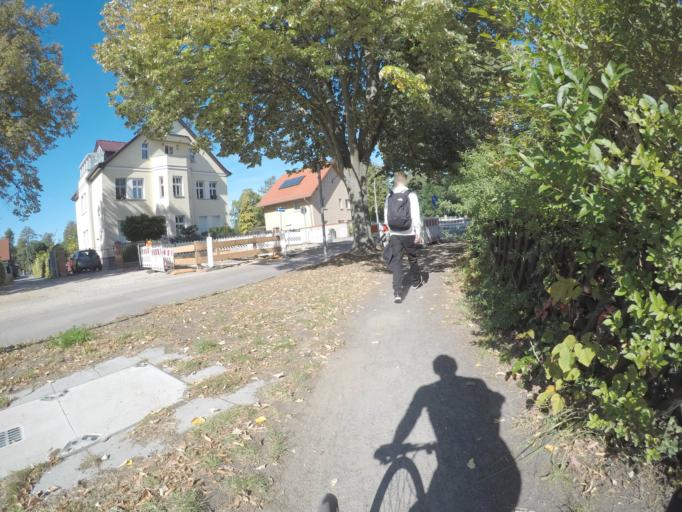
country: DE
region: Brandenburg
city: Hennigsdorf
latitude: 52.6119
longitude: 13.2173
